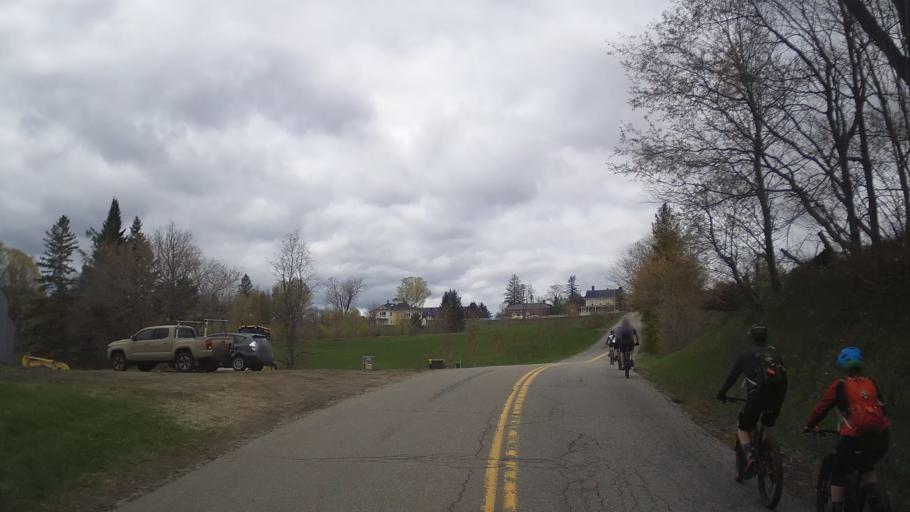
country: US
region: Vermont
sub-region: Caledonia County
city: Lyndonville
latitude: 44.5891
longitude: -71.9565
